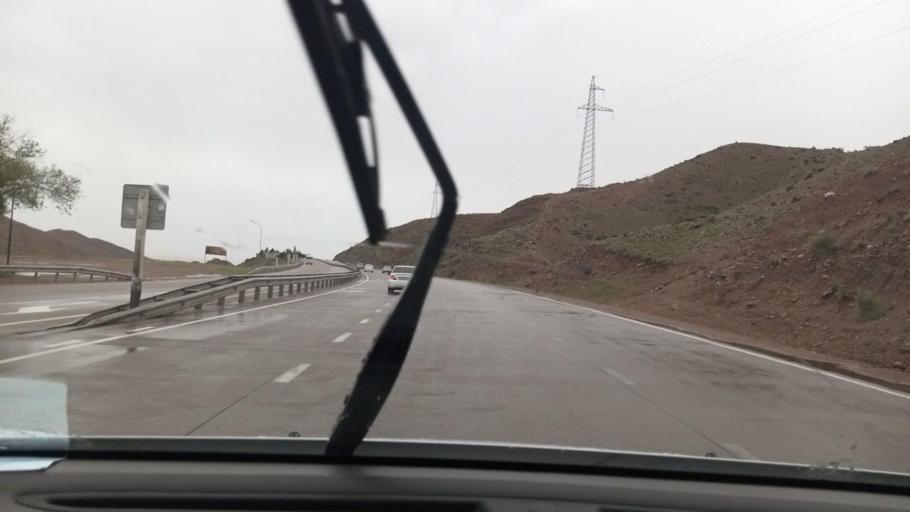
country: UZ
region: Namangan
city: Pop Shahri
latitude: 40.9469
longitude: 70.6822
